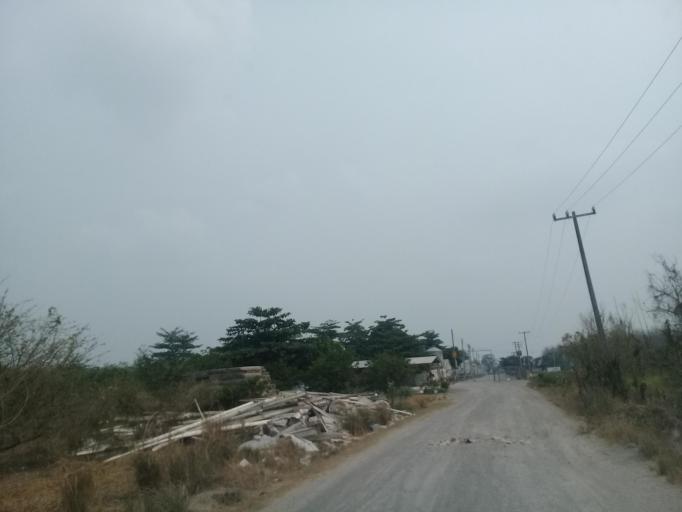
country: MX
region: Veracruz
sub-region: Medellin
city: La Laguna y Monte del Castillo
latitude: 18.9053
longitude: -96.1778
